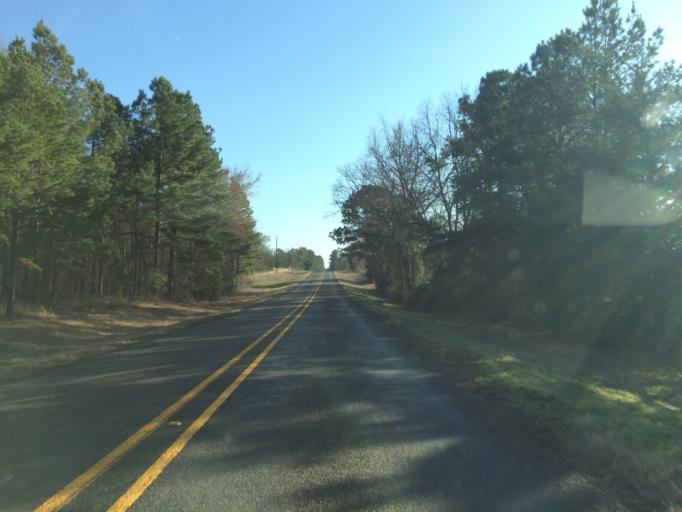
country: US
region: Texas
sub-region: Wood County
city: Hawkins
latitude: 32.6420
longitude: -95.3132
